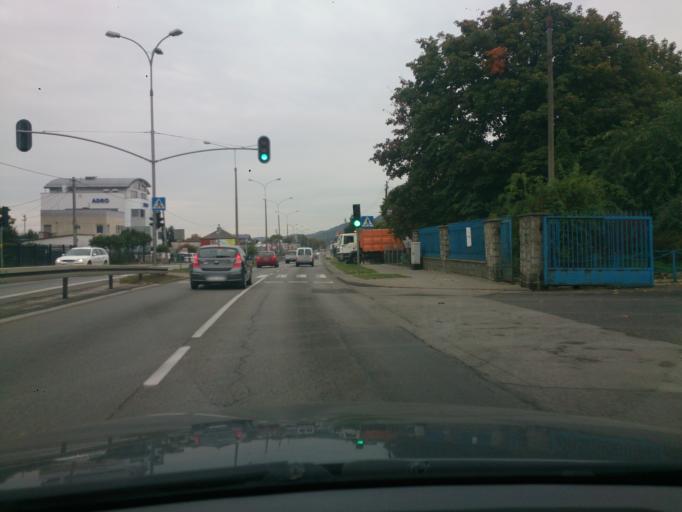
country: PL
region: Pomeranian Voivodeship
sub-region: Powiat wejherowski
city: Rumia
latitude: 54.5614
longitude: 18.3991
